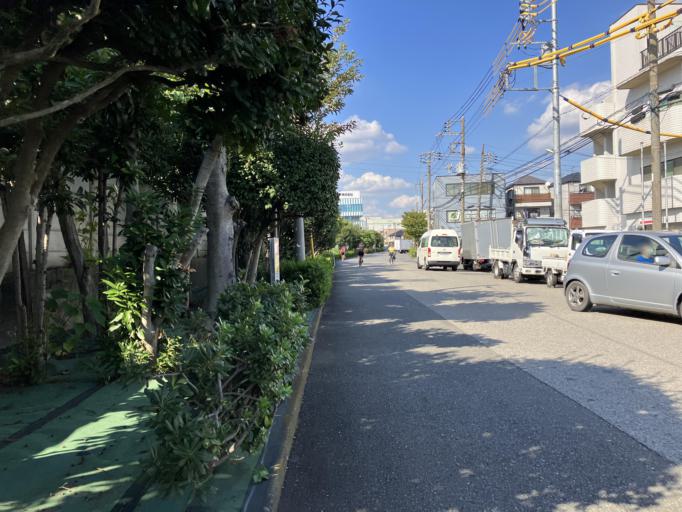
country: JP
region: Kanagawa
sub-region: Kawasaki-shi
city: Kawasaki
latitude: 35.5363
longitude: 139.7261
